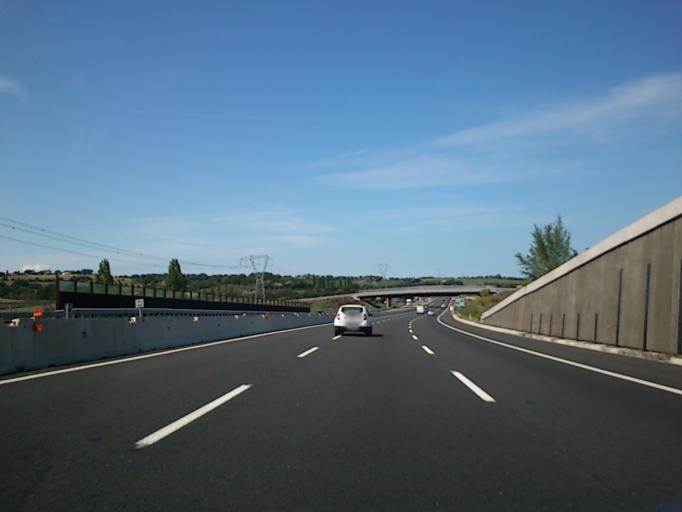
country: IT
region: The Marches
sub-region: Provincia di Pesaro e Urbino
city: Villa Ceccolini
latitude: 43.9013
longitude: 12.8312
